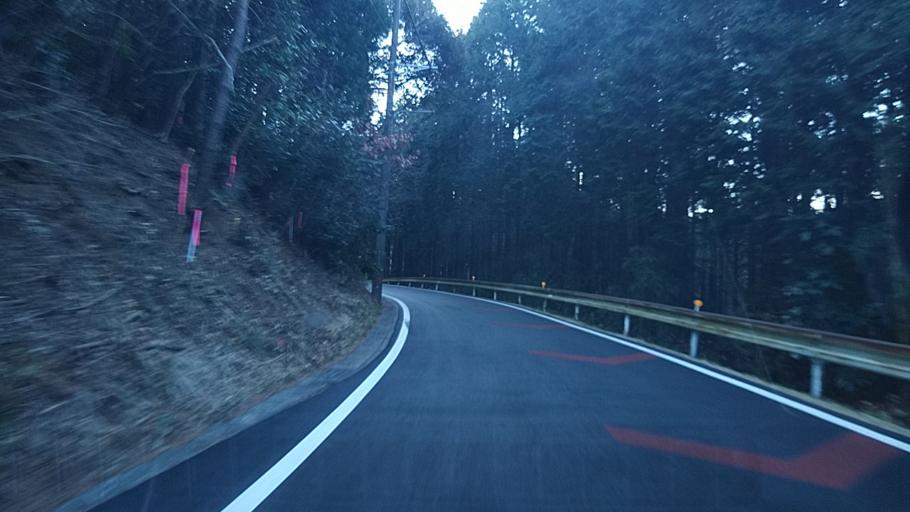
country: JP
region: Chiba
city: Kimitsu
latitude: 35.2557
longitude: 139.9505
